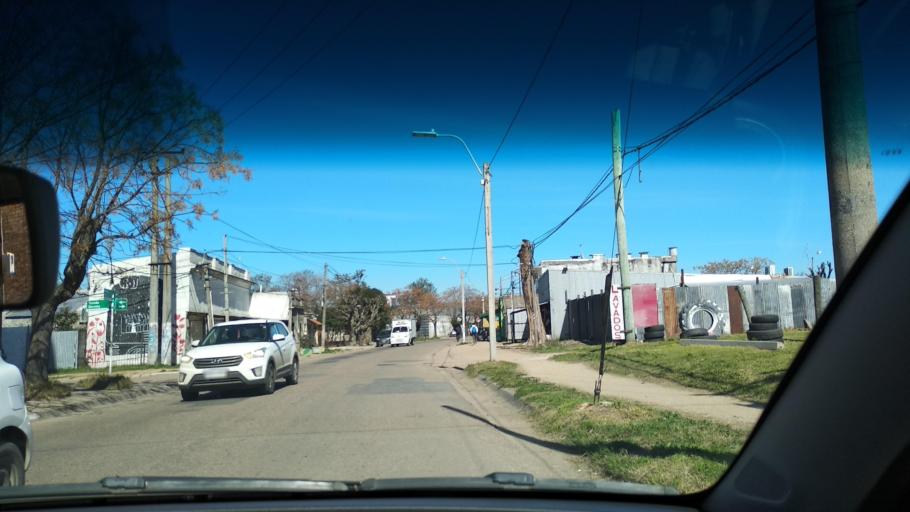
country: UY
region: Canelones
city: Las Piedras
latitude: -34.7251
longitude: -56.2102
